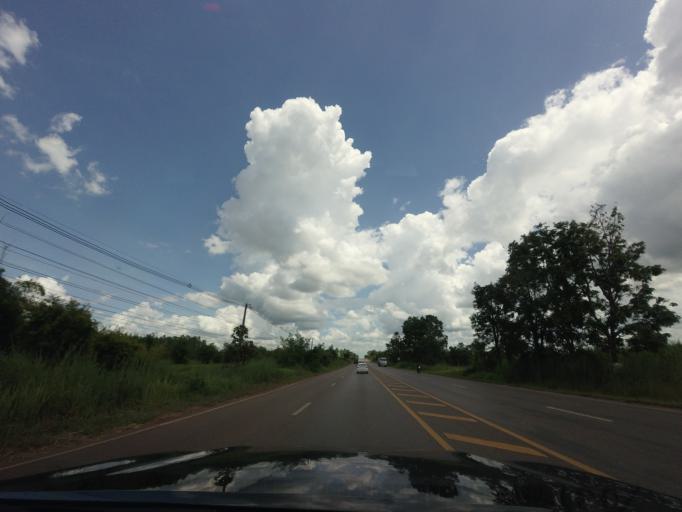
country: TH
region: Changwat Udon Thani
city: Ban Dung
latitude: 17.6854
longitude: 103.2061
